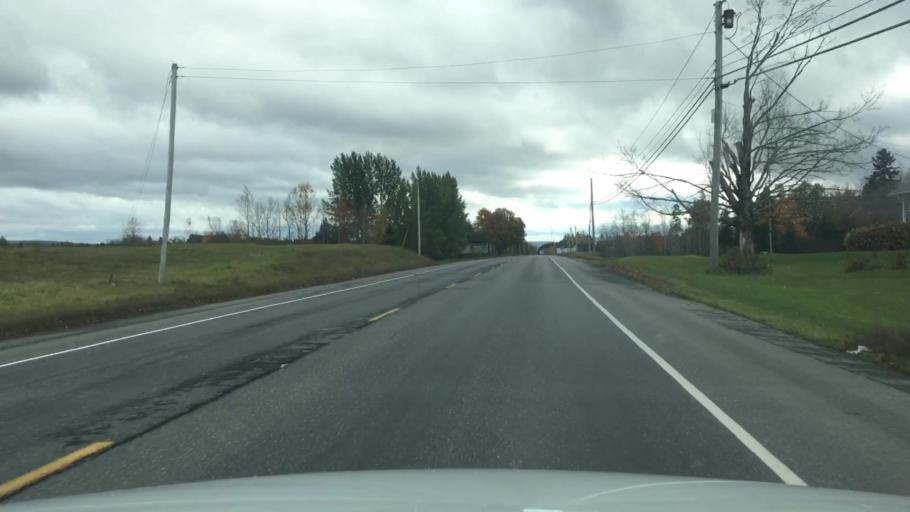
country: US
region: Maine
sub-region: Aroostook County
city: Houlton
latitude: 46.1833
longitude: -67.8411
